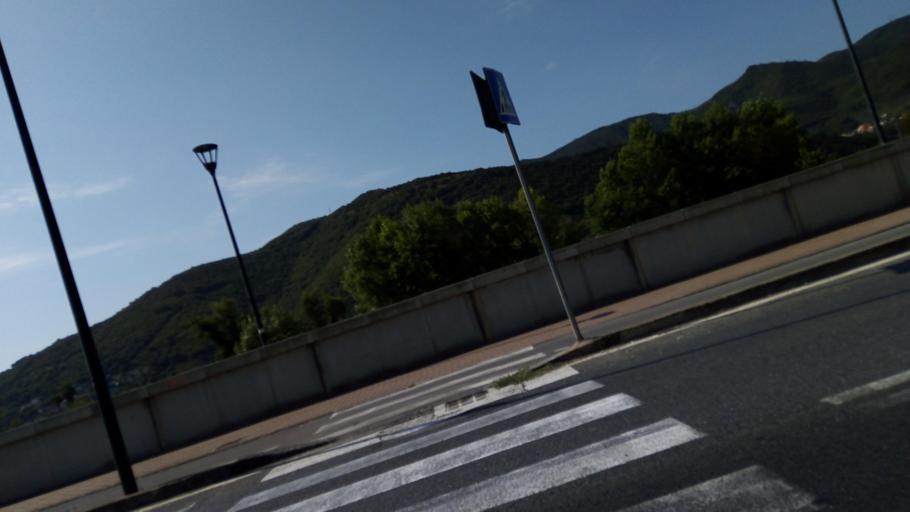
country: IT
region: Liguria
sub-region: Provincia di Savona
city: Campochiesa
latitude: 44.0539
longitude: 8.1979
